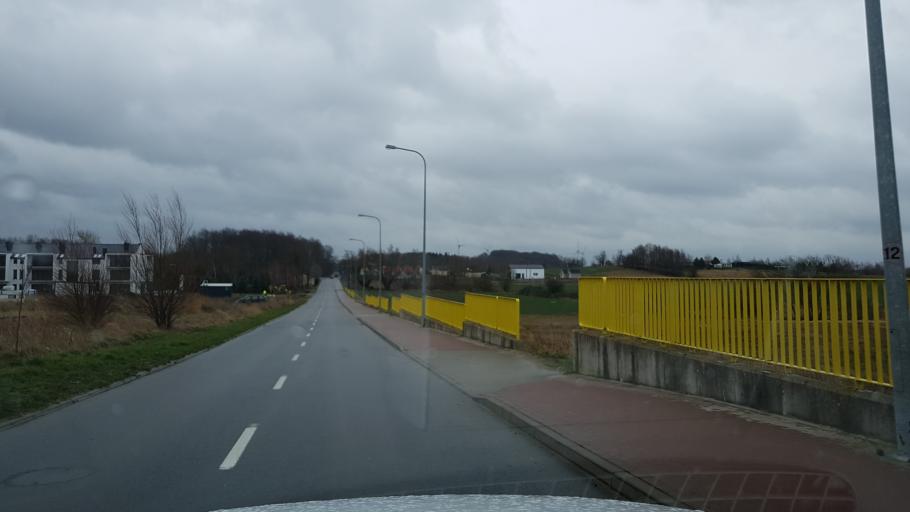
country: PL
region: West Pomeranian Voivodeship
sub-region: Powiat kolobrzeski
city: Ustronie Morskie
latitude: 54.2109
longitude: 15.7652
